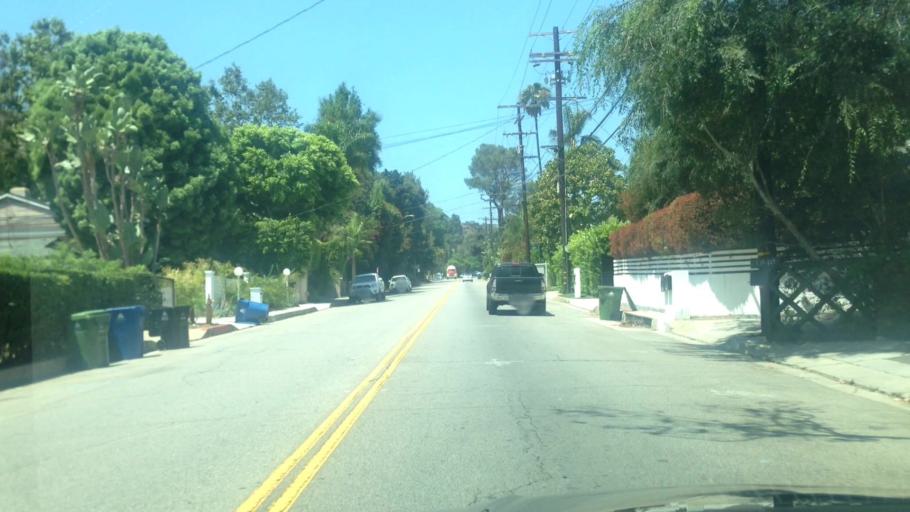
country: US
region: California
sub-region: Los Angeles County
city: Beverly Hills
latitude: 34.1062
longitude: -118.4055
